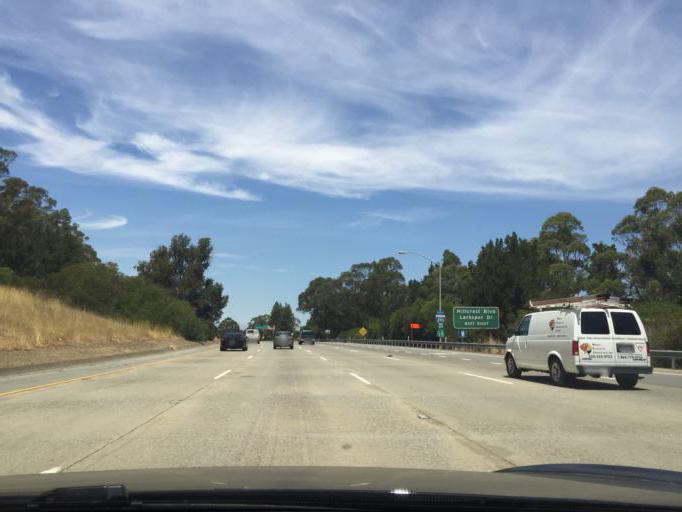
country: US
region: California
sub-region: San Mateo County
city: Millbrae
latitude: 37.5840
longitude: -122.4060
